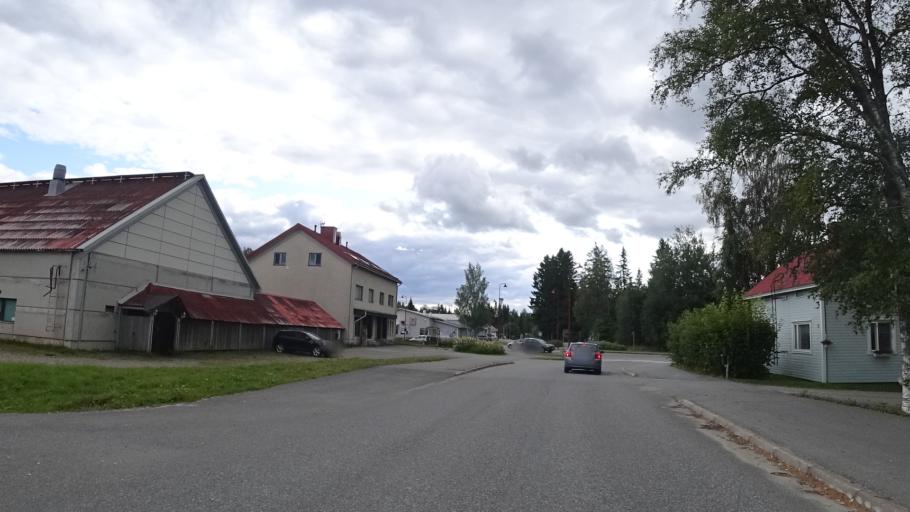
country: FI
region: North Karelia
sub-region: Joensuu
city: Ilomantsi
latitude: 62.6695
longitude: 30.9379
